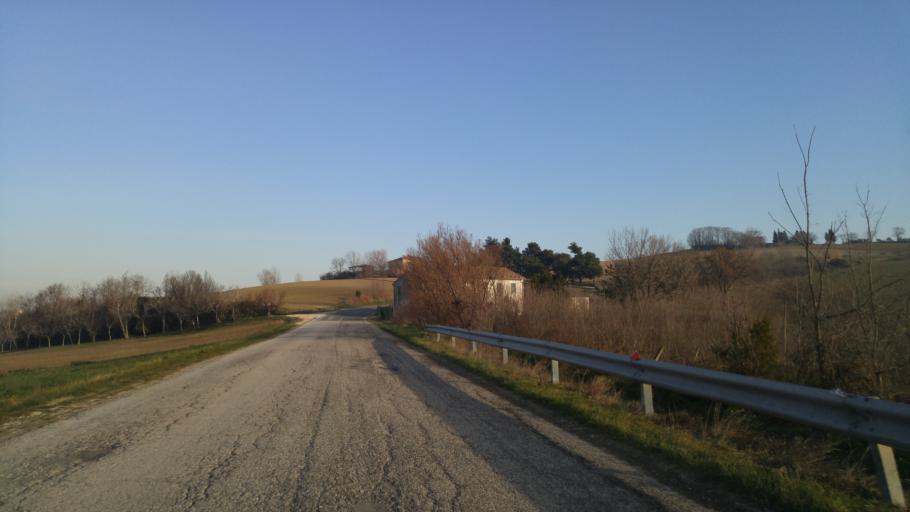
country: IT
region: The Marches
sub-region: Provincia di Pesaro e Urbino
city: San Giorgio di Pesaro
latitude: 43.7099
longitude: 13.0100
